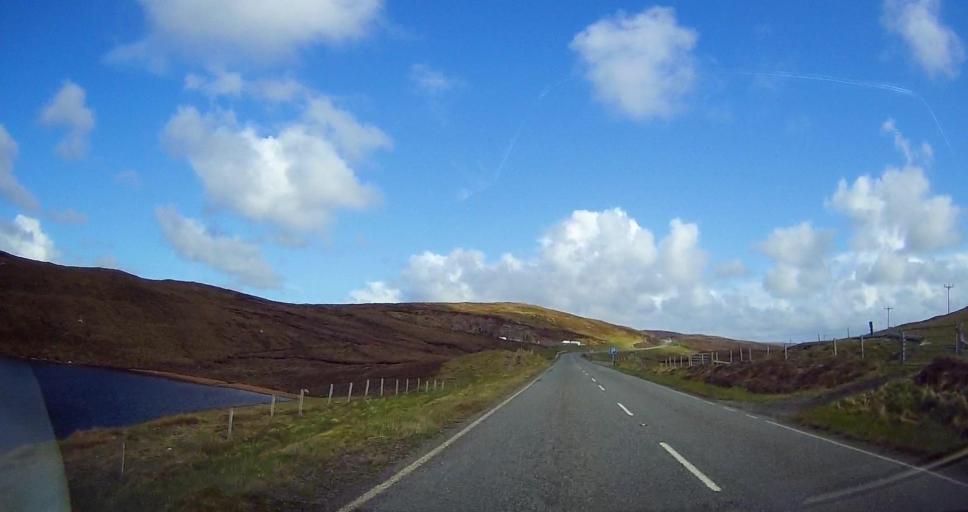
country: GB
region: Scotland
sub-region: Shetland Islands
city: Lerwick
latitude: 60.4438
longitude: -1.3954
